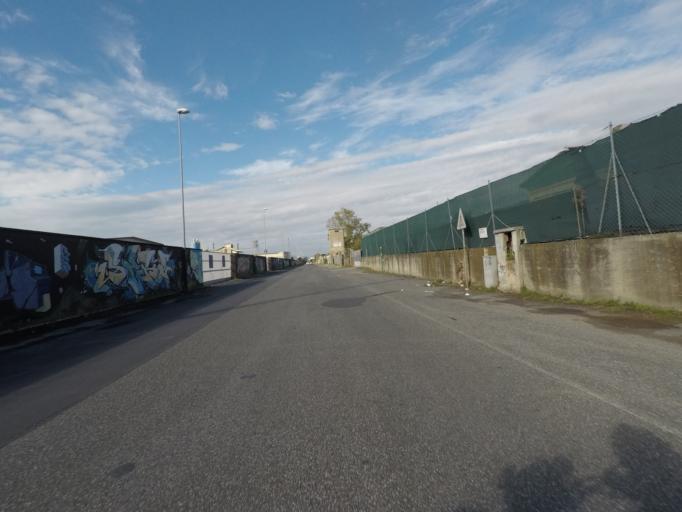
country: IT
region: Tuscany
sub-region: Provincia di Massa-Carrara
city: Massa
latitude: 44.0299
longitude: 10.1100
